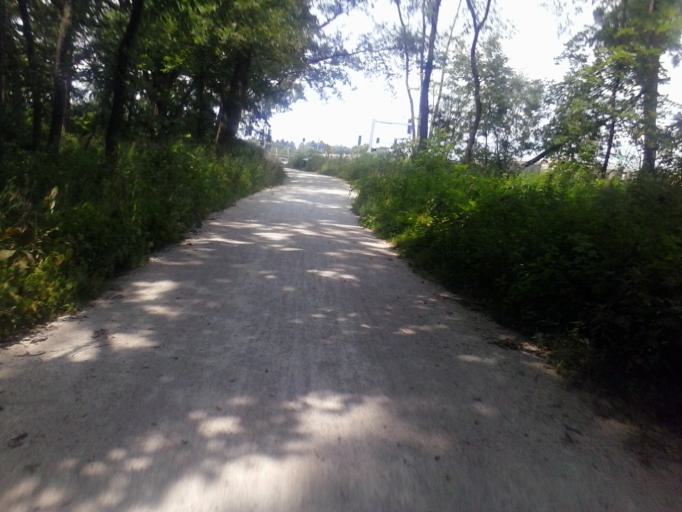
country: US
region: Illinois
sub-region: DuPage County
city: Warrenville
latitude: 41.8308
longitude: -88.1465
